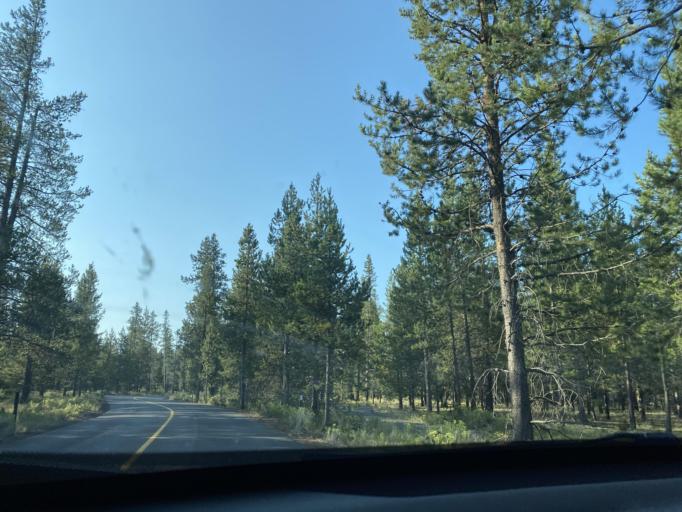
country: US
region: Oregon
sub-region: Deschutes County
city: Sunriver
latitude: 43.8953
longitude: -121.4392
